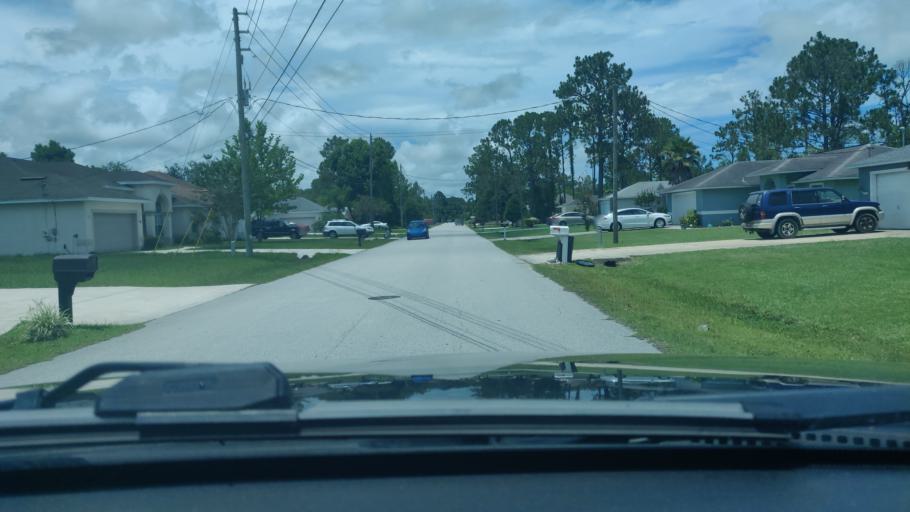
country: US
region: Florida
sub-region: Flagler County
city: Bunnell
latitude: 29.5195
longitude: -81.2563
